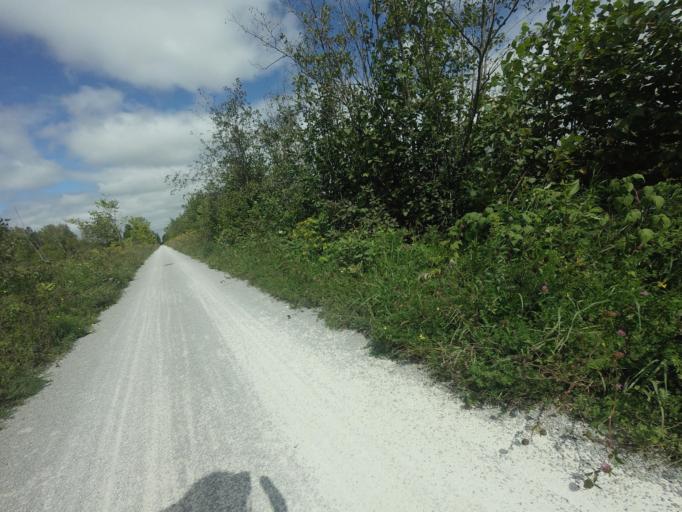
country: CA
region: Ontario
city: Uxbridge
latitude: 44.1538
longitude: -79.0822
